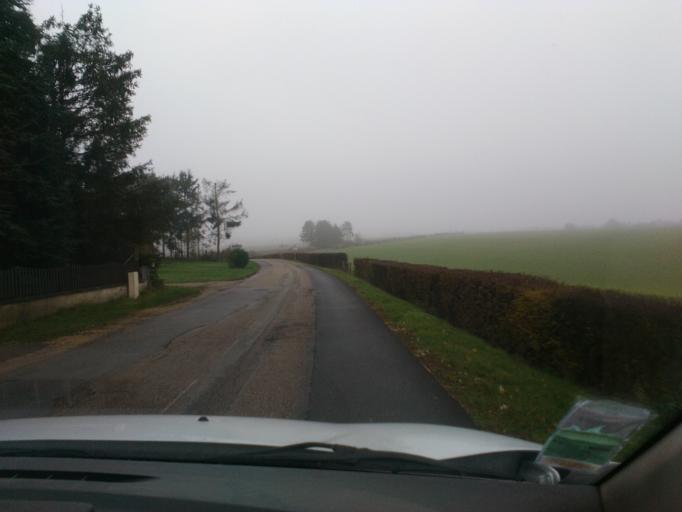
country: FR
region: Lorraine
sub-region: Departement des Vosges
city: Neufchateau
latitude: 48.3558
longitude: 5.7321
